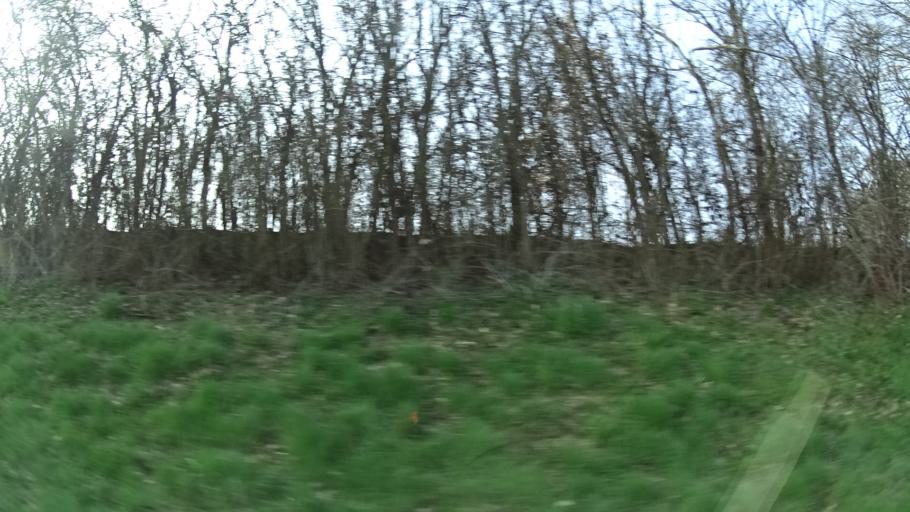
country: DE
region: Rheinland-Pfalz
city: Niederstaufenbach
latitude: 49.5262
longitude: 7.5156
